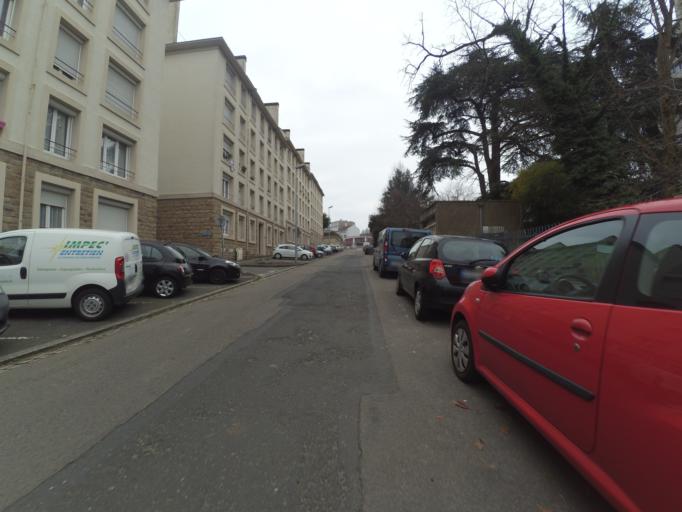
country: FR
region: Pays de la Loire
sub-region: Departement de la Loire-Atlantique
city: Nantes
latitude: 47.2257
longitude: -1.5757
